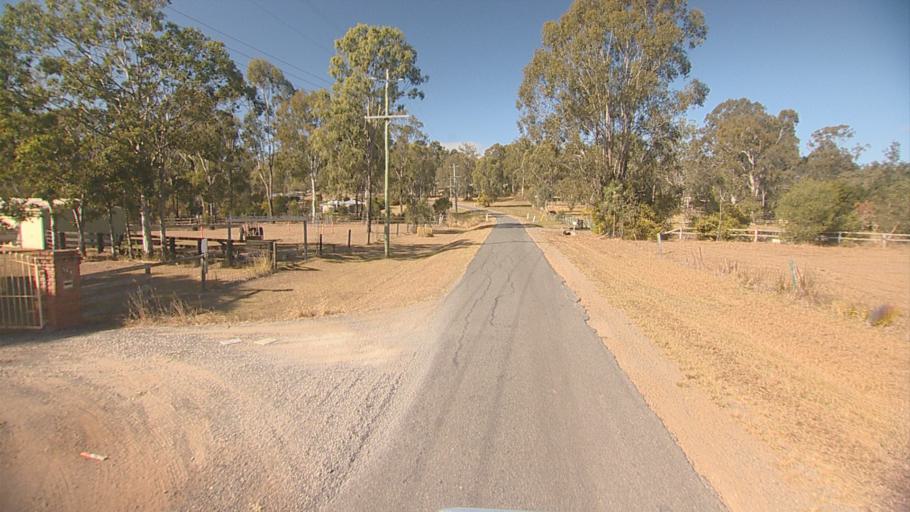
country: AU
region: Queensland
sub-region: Logan
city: Cedar Vale
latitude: -27.8477
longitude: 152.9883
